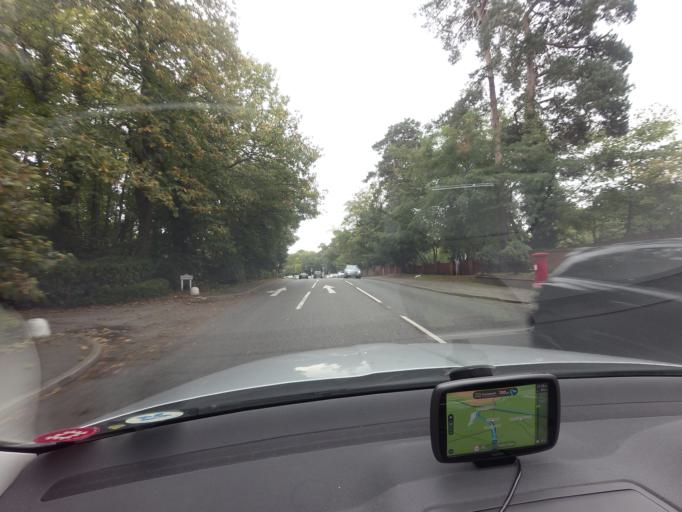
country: GB
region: England
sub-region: Surrey
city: Cobham
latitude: 51.3358
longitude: -0.4361
